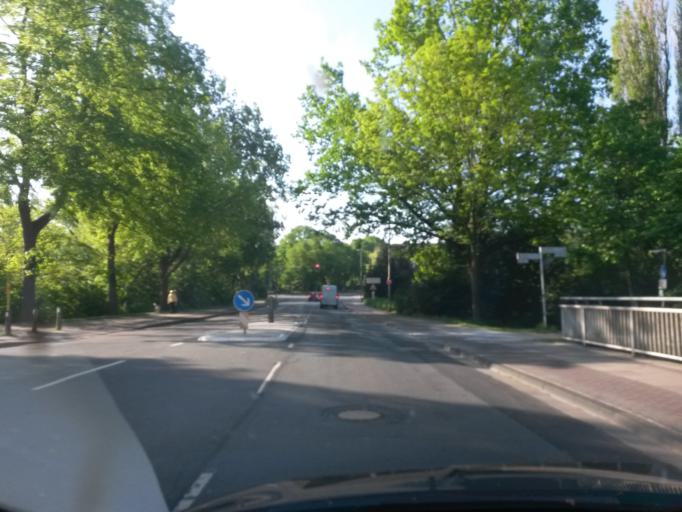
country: DE
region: North Rhine-Westphalia
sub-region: Regierungsbezirk Detmold
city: Bielefeld
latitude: 52.0229
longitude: 8.5658
